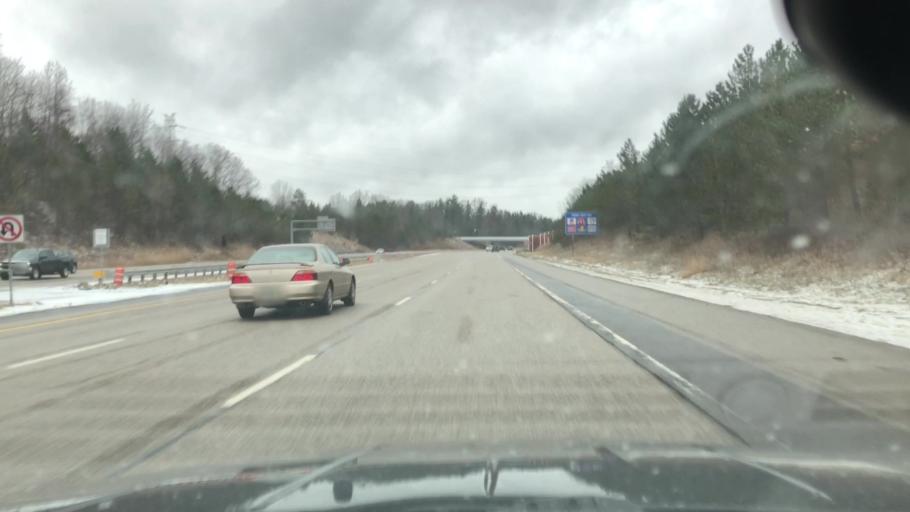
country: US
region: Ohio
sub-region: Cuyahoga County
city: Brecksville
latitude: 41.3037
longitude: -81.6460
